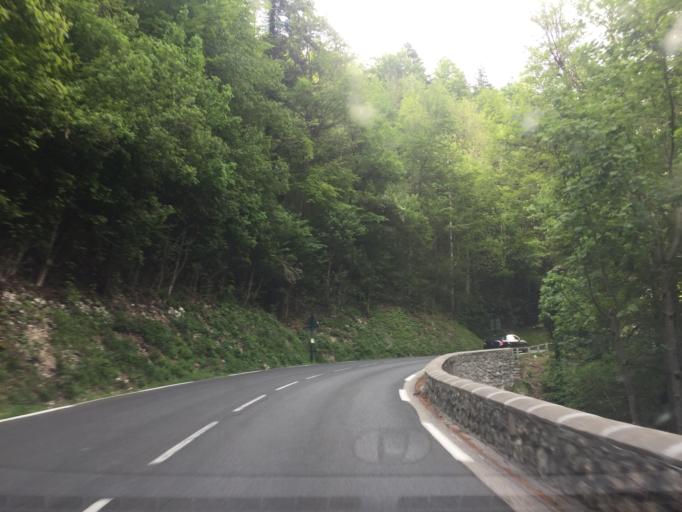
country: FR
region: Rhone-Alpes
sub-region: Departement de l'Isere
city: Saint-Laurent-du-Pont
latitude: 45.3498
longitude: 5.7822
